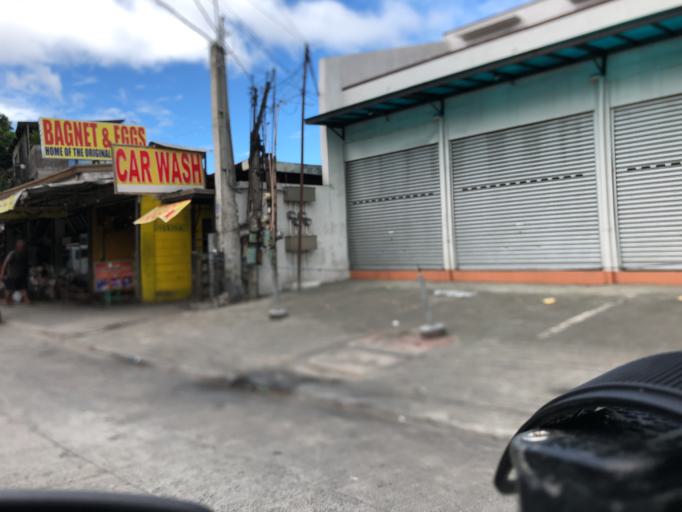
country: PH
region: Central Luzon
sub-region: Province of Bulacan
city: San Jose del Monte
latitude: 14.7386
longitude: 121.0576
